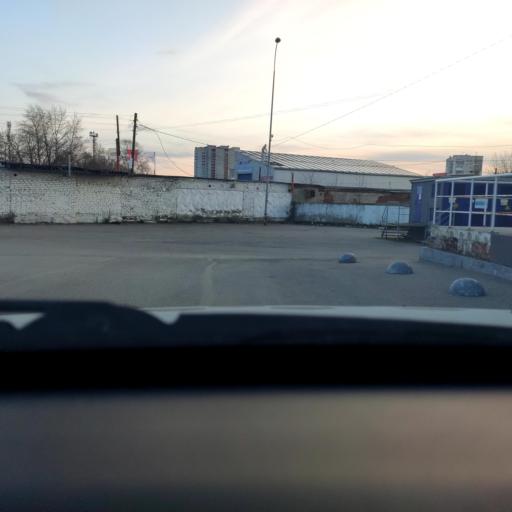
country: RU
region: Perm
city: Perm
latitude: 57.9807
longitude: 56.2412
